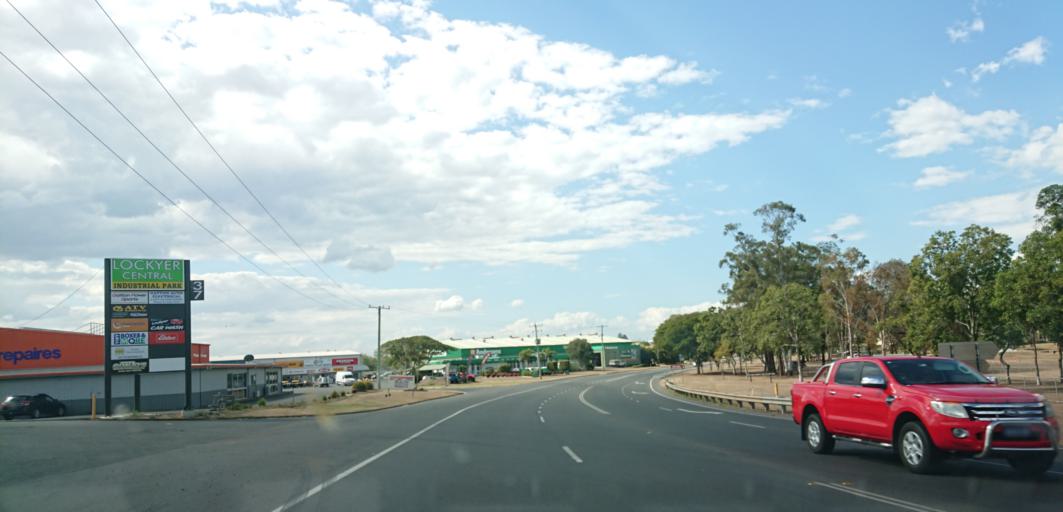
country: AU
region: Queensland
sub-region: Lockyer Valley
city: Gatton
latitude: -27.5708
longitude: 152.2662
